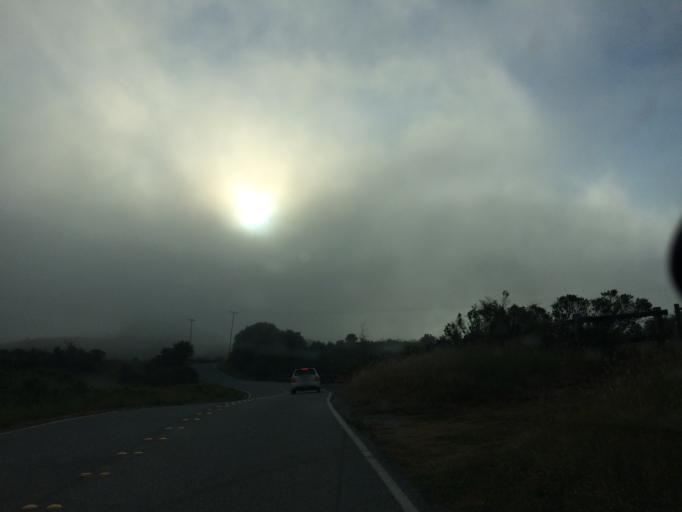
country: US
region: California
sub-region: Santa Clara County
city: Los Altos Hills
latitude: 37.3260
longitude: -122.1785
